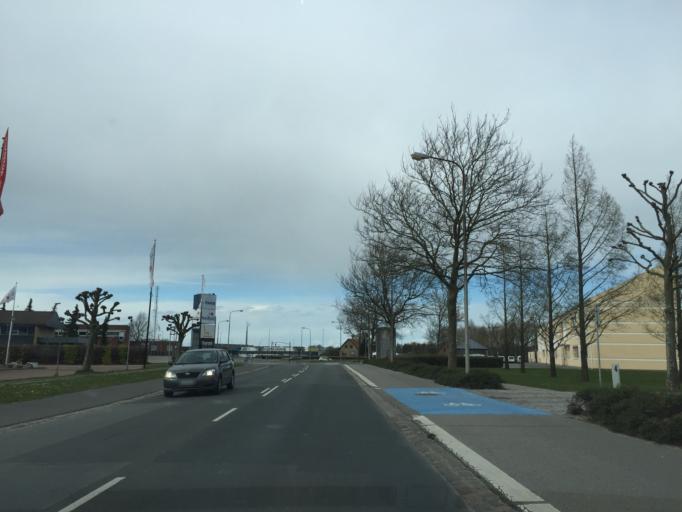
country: DK
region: South Denmark
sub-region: Odense Kommune
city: Neder Holluf
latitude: 55.3896
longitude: 10.4391
